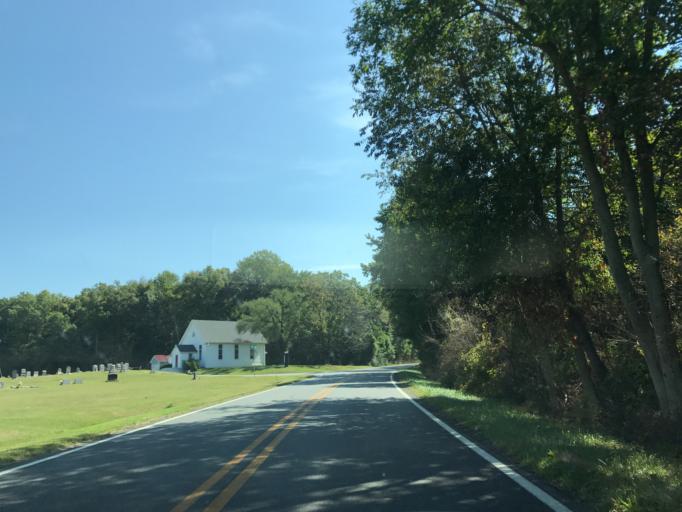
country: US
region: Delaware
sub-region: New Castle County
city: Townsend
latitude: 39.2997
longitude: -75.7481
